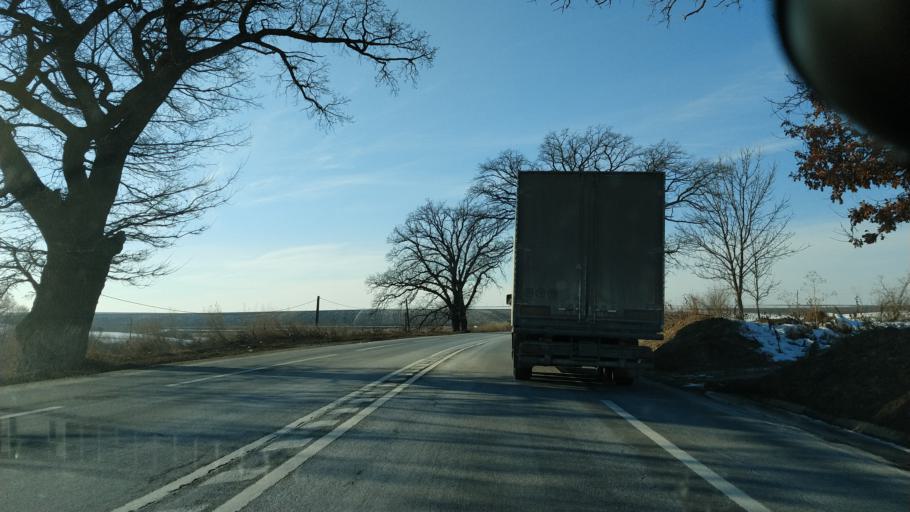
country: RO
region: Iasi
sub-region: Comuna Butea
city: Butea
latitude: 47.1109
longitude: 26.9324
